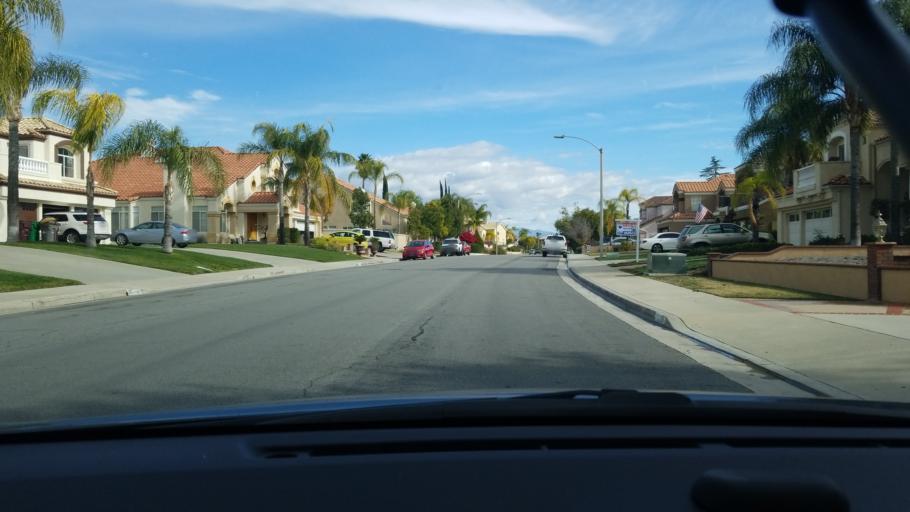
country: US
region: California
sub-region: Riverside County
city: Murrieta
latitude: 33.5963
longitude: -117.1996
